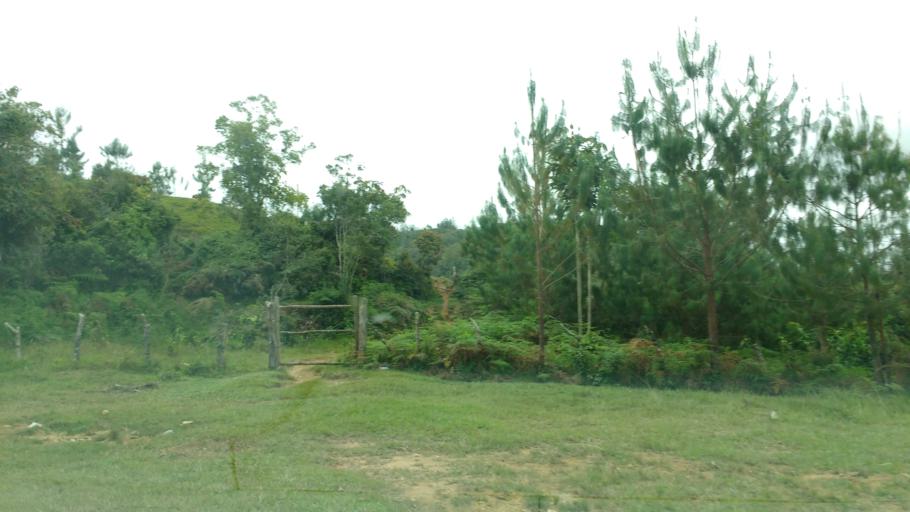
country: CO
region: Antioquia
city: Concepcion
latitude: 6.3665
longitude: -75.2233
